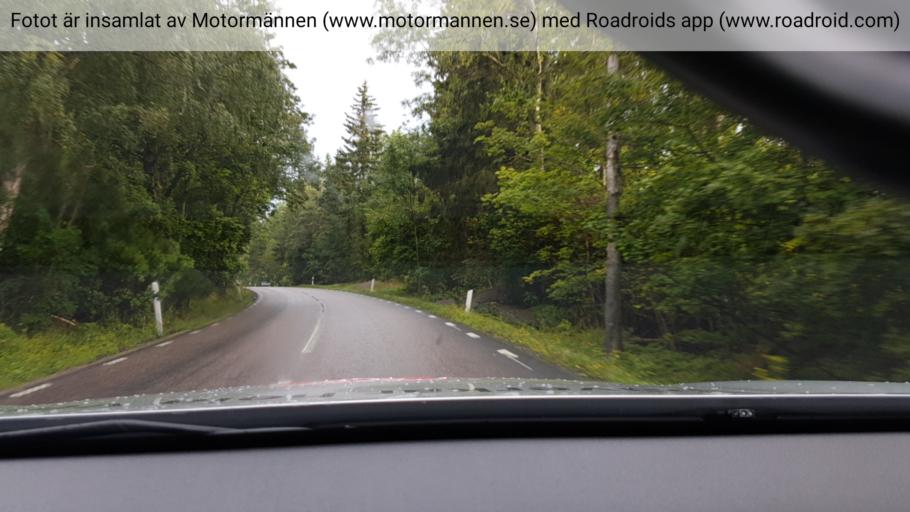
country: SE
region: Uppsala
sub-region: Osthammars Kommun
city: Marieberg
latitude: 60.1051
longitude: 18.4581
